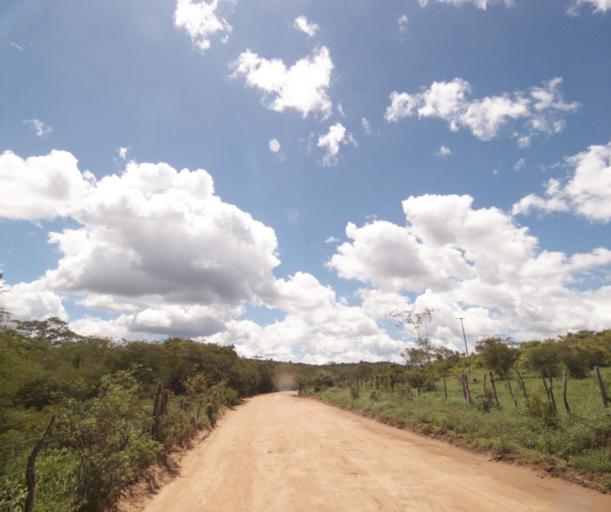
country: BR
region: Bahia
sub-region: Pocoes
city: Pocoes
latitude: -14.3797
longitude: -40.5632
